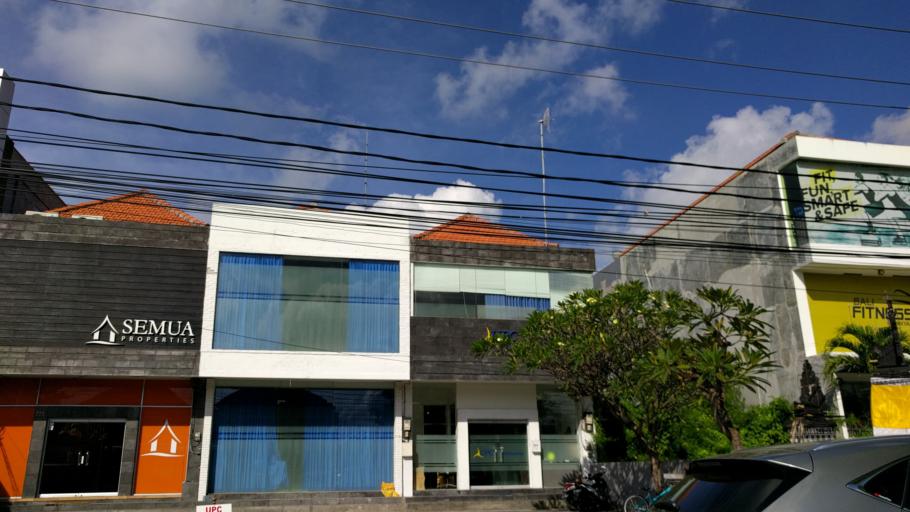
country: ID
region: Bali
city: Kuta
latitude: -8.6877
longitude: 115.1712
